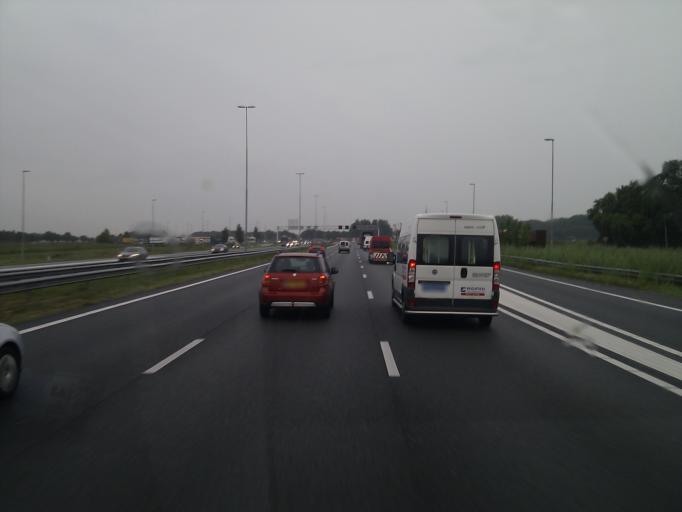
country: NL
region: Gelderland
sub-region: Gemeente Maasdriel
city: Hedel
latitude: 51.7801
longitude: 5.2582
